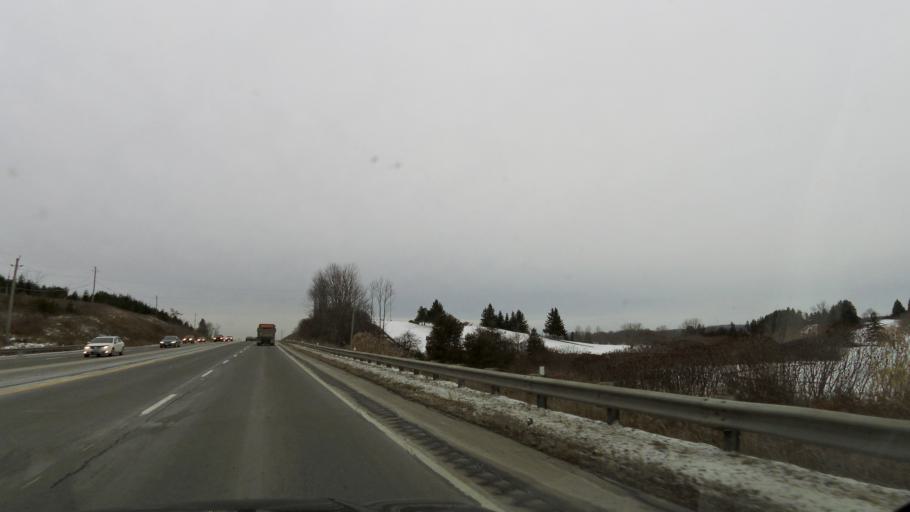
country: CA
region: Ontario
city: Newmarket
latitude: 44.0370
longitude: -79.5603
